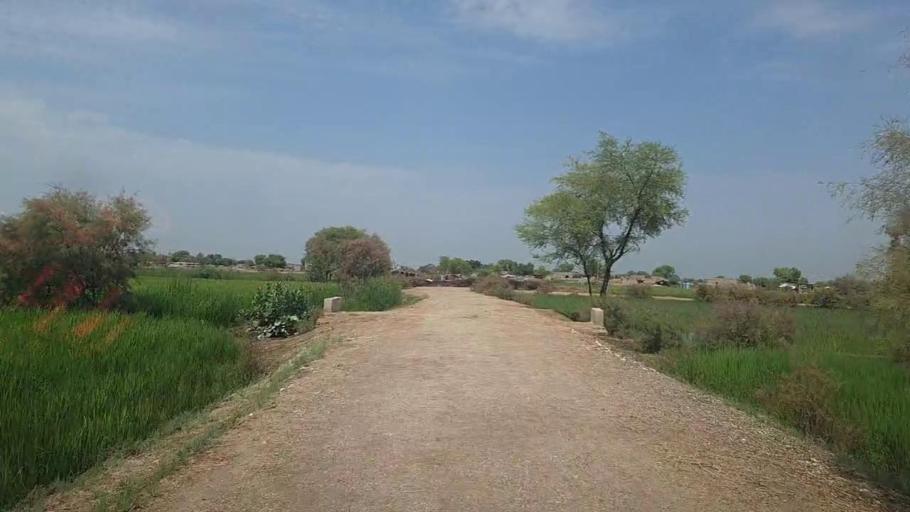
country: PK
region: Sindh
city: Thul
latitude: 28.3055
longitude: 68.6821
